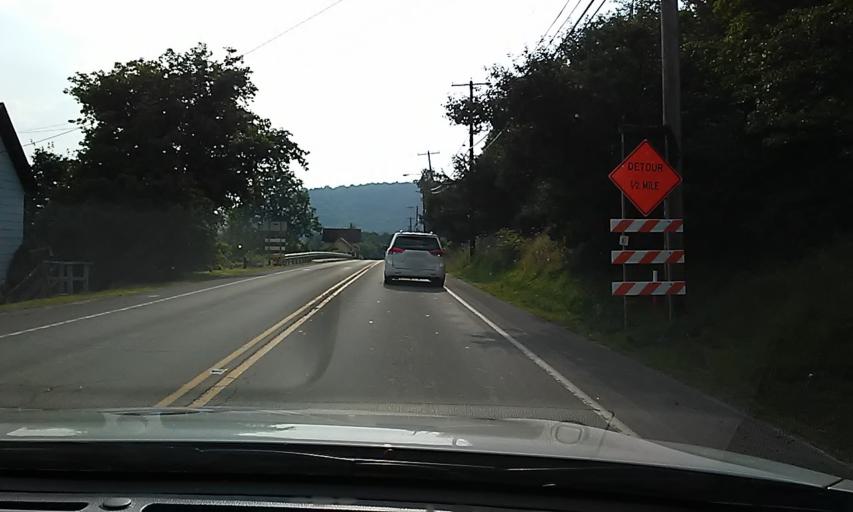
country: US
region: Pennsylvania
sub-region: Potter County
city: Coudersport
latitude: 41.7746
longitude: -78.0101
